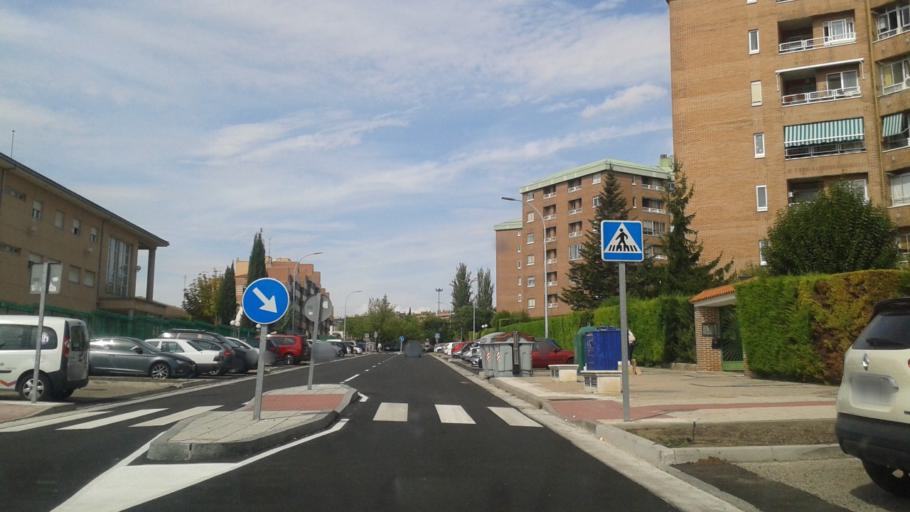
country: ES
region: Castille and Leon
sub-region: Provincia de Valladolid
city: Zaratan
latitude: 41.6325
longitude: -4.7587
